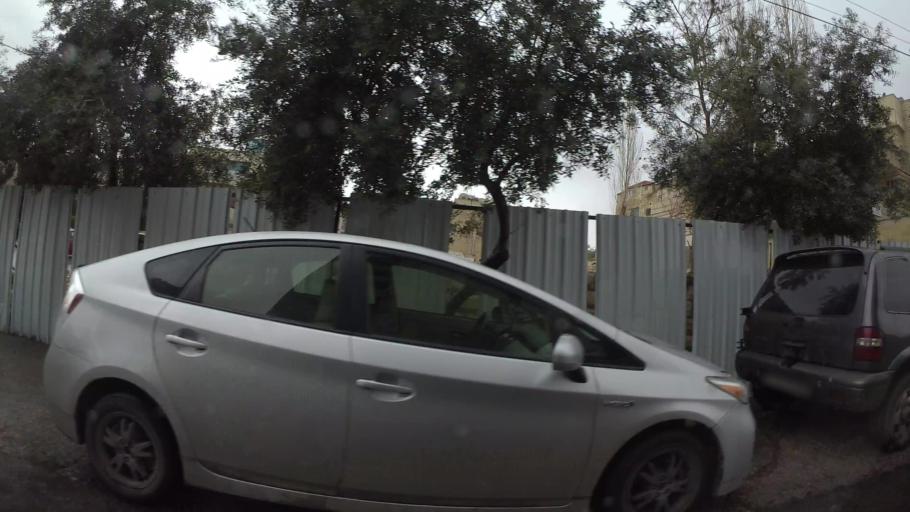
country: JO
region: Amman
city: Amman
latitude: 31.9630
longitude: 35.9015
